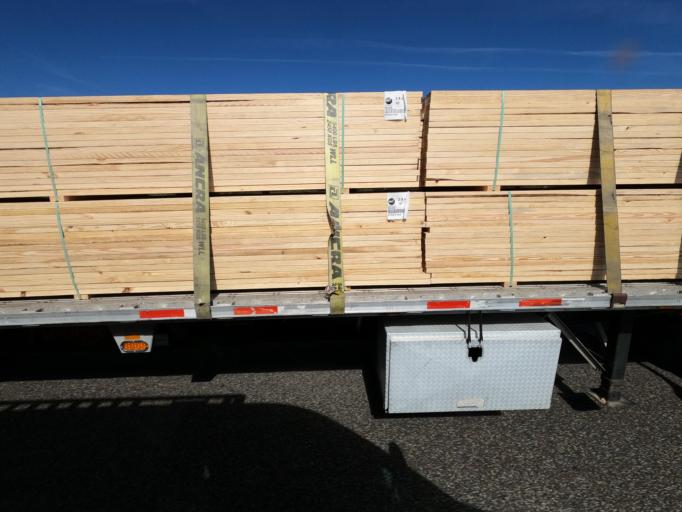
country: US
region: Tennessee
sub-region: Crockett County
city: Bells
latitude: 35.5876
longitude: -89.0832
